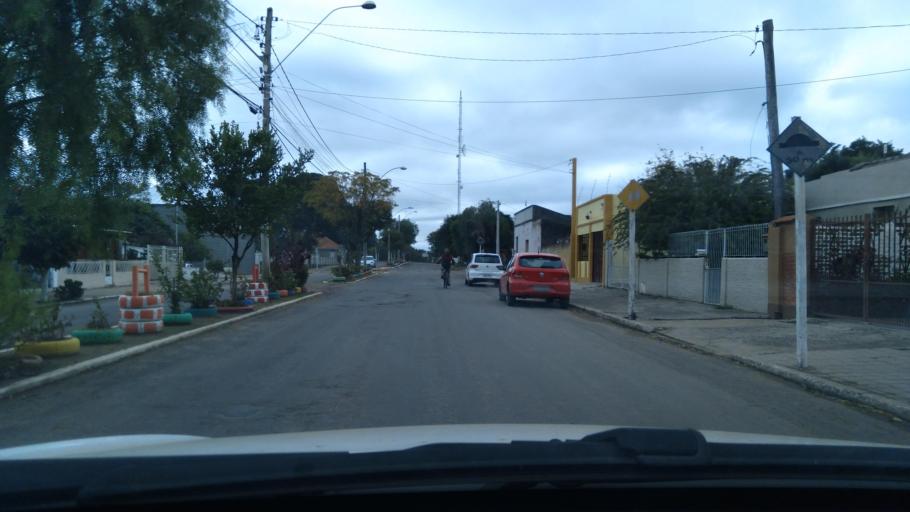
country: BR
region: Rio Grande do Sul
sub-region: Dom Pedrito
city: Dom Pedrito
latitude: -30.9692
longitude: -54.6728
